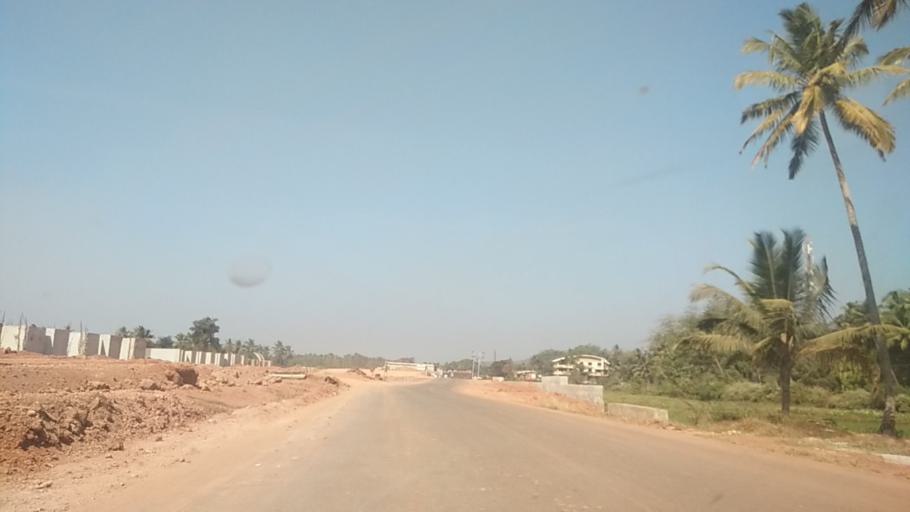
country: IN
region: Goa
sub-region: South Goa
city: Raia
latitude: 15.3044
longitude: 73.9462
